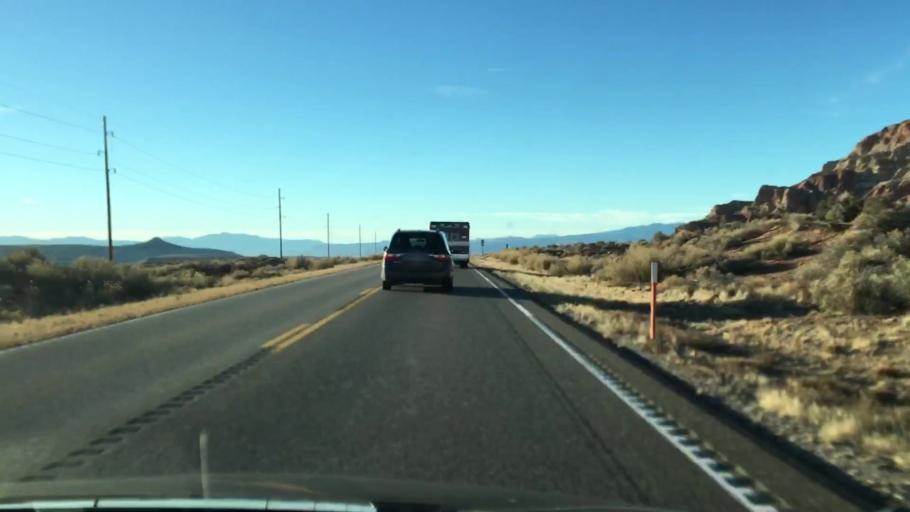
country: US
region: Utah
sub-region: Washington County
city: Hurricane
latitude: 37.1295
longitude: -113.2219
